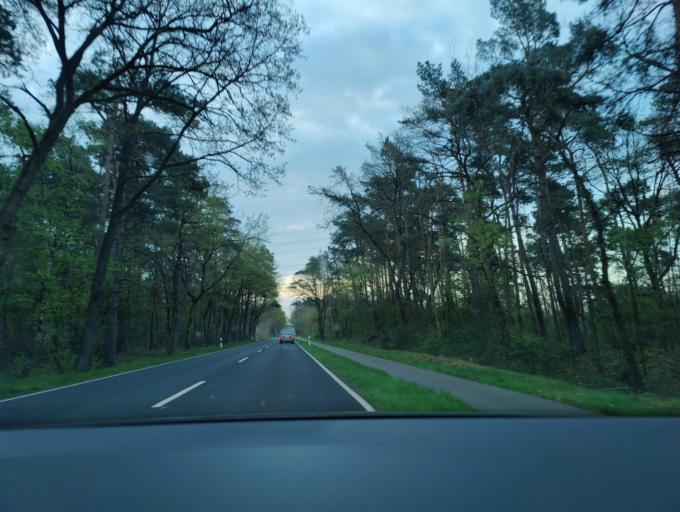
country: DE
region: Lower Saxony
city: Emsburen
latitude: 52.4576
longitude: 7.2940
